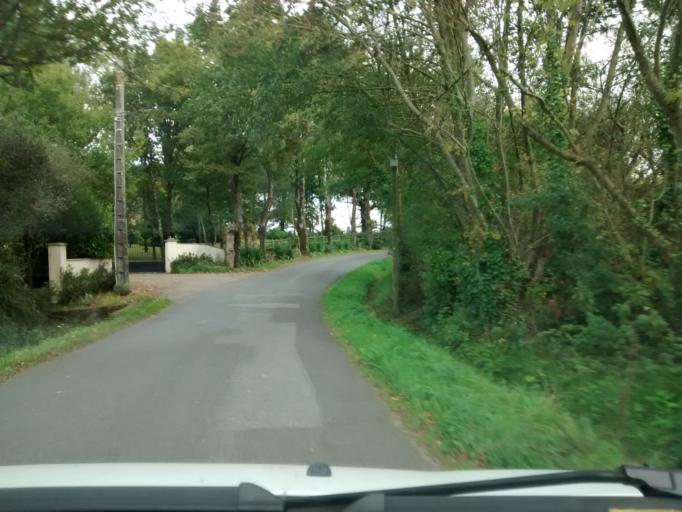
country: FR
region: Pays de la Loire
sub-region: Departement de la Loire-Atlantique
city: Coueron
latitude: 47.2361
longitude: -1.6986
